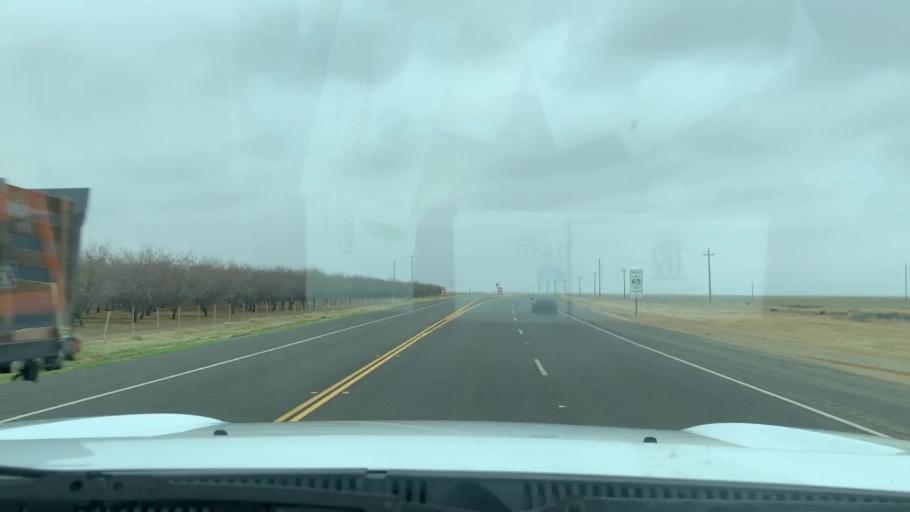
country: US
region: California
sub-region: Kern County
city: Lost Hills
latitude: 35.6157
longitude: -119.7565
